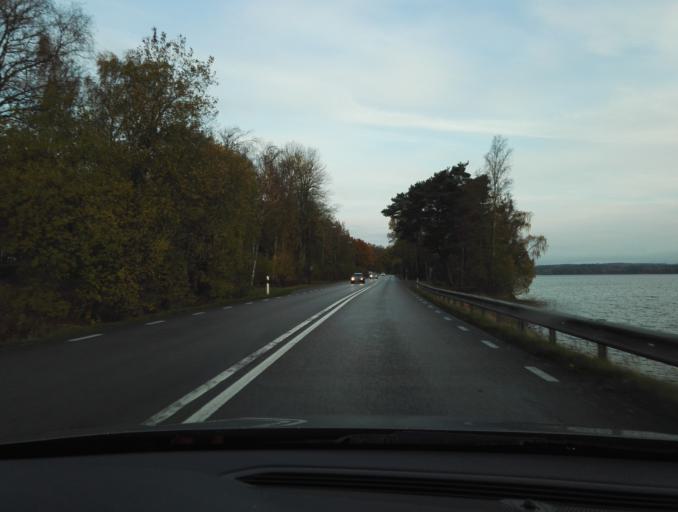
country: SE
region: Kronoberg
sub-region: Alvesta Kommun
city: Moheda
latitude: 56.9846
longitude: 14.6950
